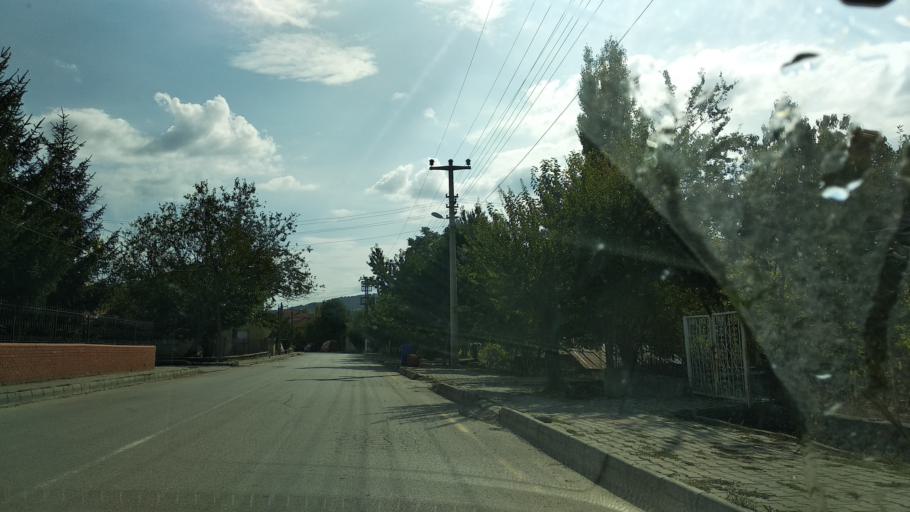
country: TR
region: Bolu
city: Seben
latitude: 40.4107
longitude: 31.5704
